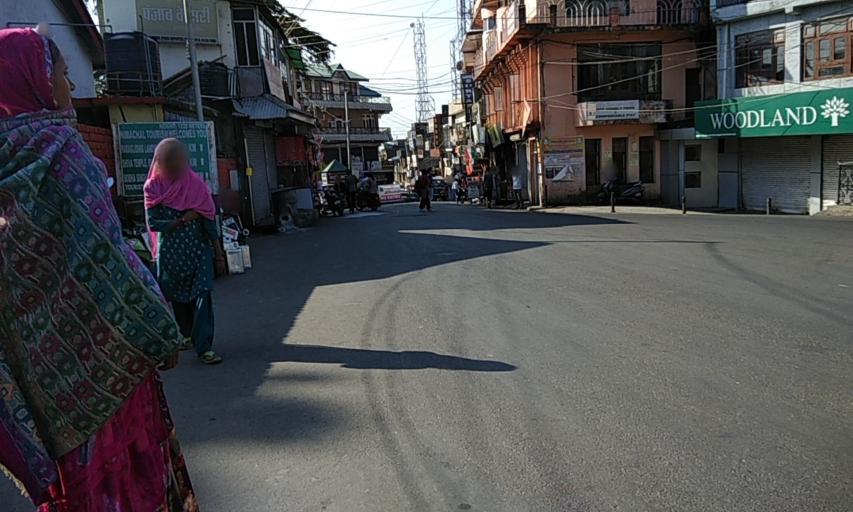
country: IN
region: Himachal Pradesh
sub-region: Kangra
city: Palampur
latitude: 32.1110
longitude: 76.5363
